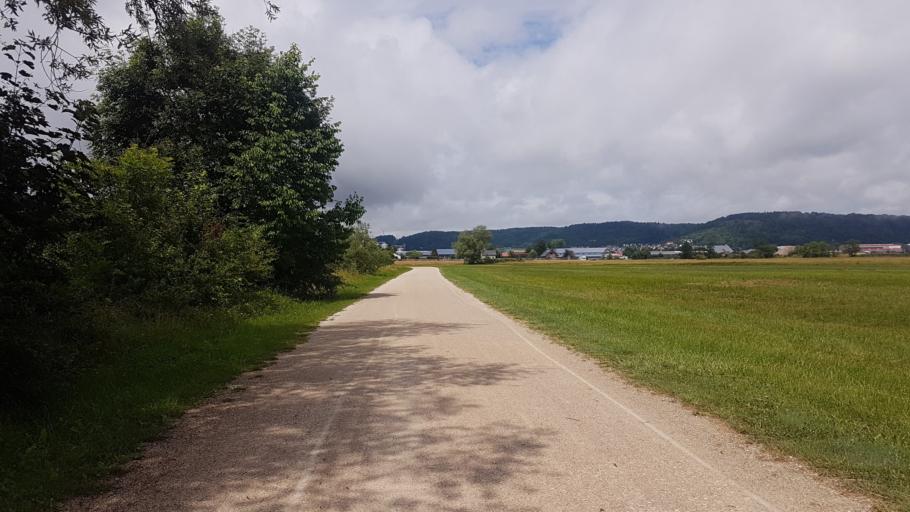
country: DE
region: Bavaria
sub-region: Upper Palatinate
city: Dietfurt
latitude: 49.0185
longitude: 11.5968
